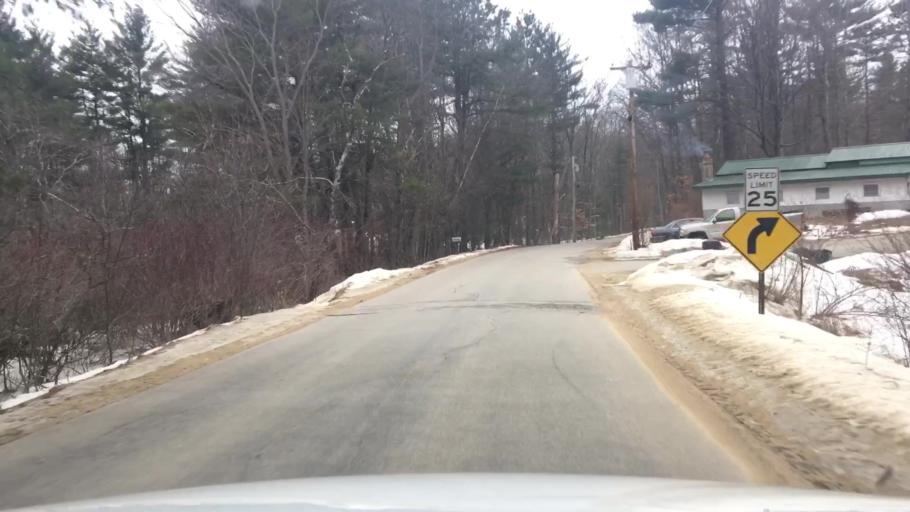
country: US
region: New Hampshire
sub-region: Strafford County
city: Rochester
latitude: 43.3483
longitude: -70.9626
